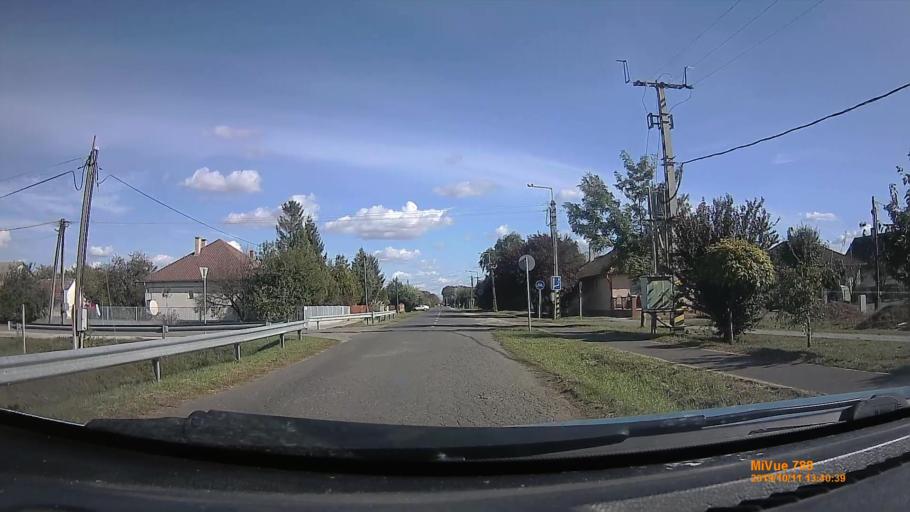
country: HU
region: Hajdu-Bihar
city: Balmazujvaros
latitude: 47.5396
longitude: 21.3372
